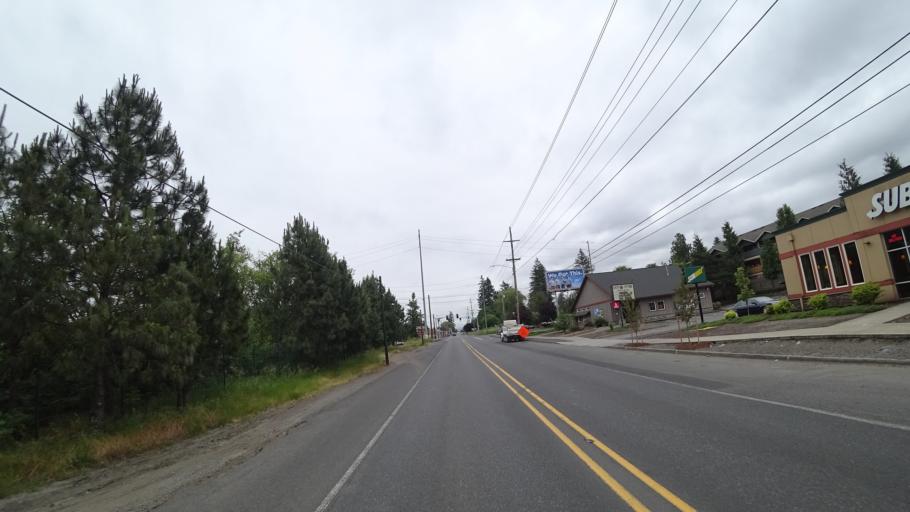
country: US
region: Oregon
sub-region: Multnomah County
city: Fairview
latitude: 45.5498
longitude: -122.4973
